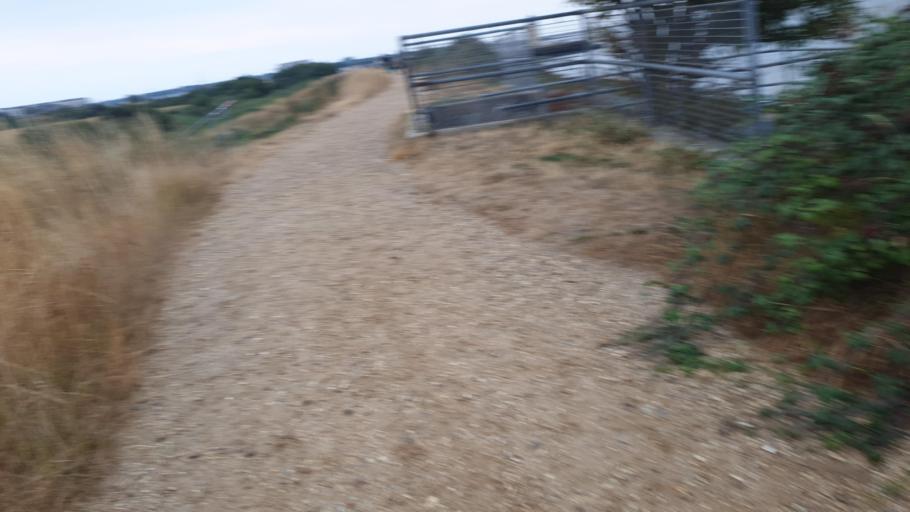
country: GB
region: England
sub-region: Essex
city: Brightlingsea
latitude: 51.8077
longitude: 1.0081
